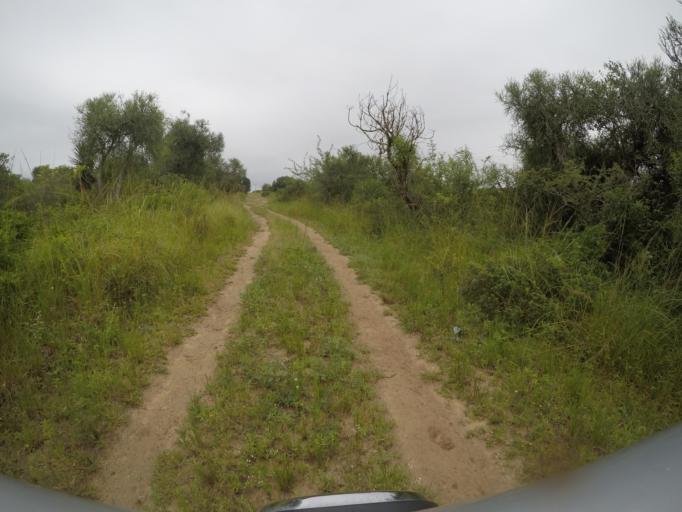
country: ZA
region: KwaZulu-Natal
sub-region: uThungulu District Municipality
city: Empangeni
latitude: -28.6070
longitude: 31.8380
